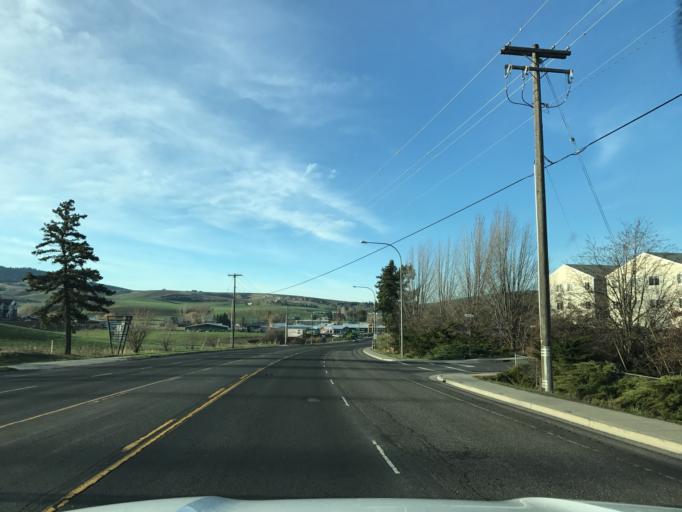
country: US
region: Idaho
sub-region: Latah County
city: Moscow
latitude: 46.7202
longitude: -117.0015
